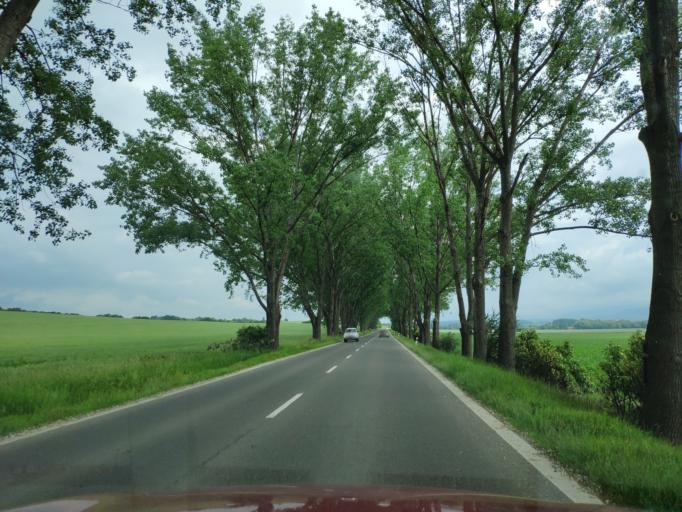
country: SK
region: Kosicky
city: Kosice
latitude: 48.8106
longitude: 21.3008
